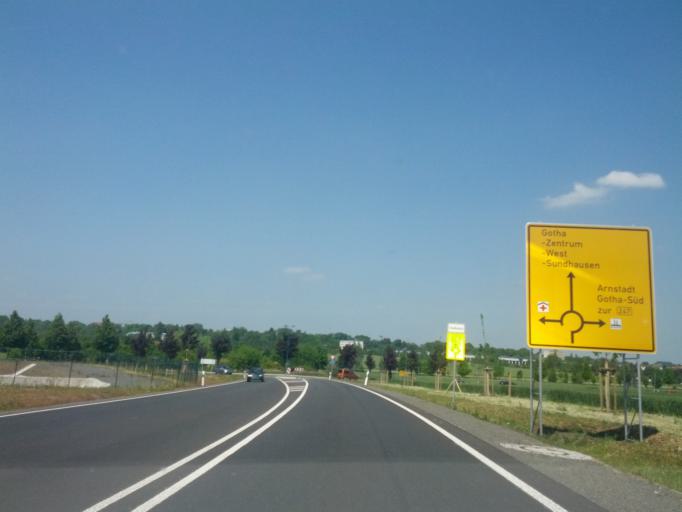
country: DE
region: Thuringia
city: Gotha
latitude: 50.9278
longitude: 10.6826
